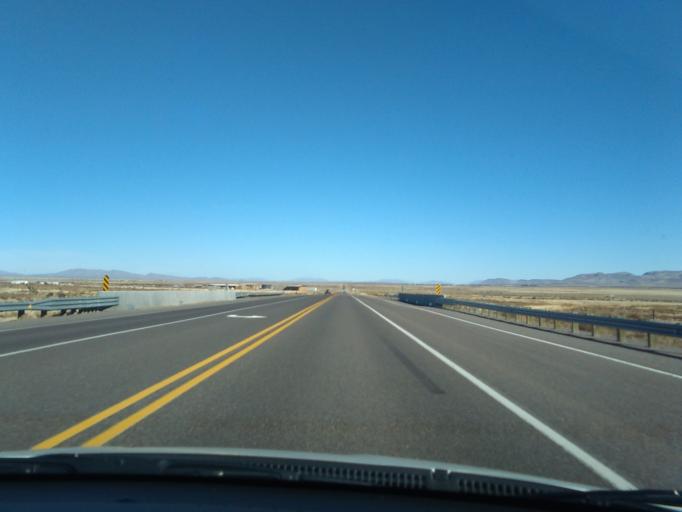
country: US
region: New Mexico
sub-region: Dona Ana County
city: Hatch
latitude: 32.5800
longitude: -107.3854
